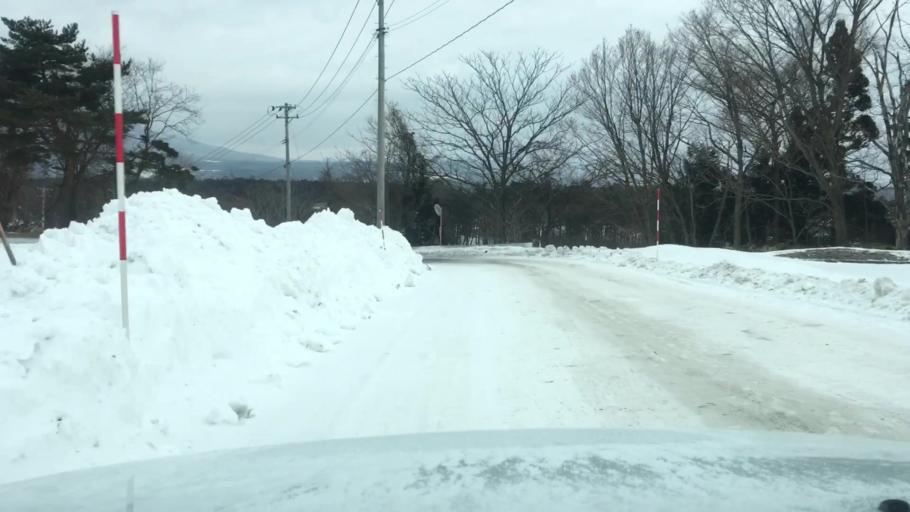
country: JP
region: Iwate
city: Shizukuishi
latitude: 39.9106
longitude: 141.0055
